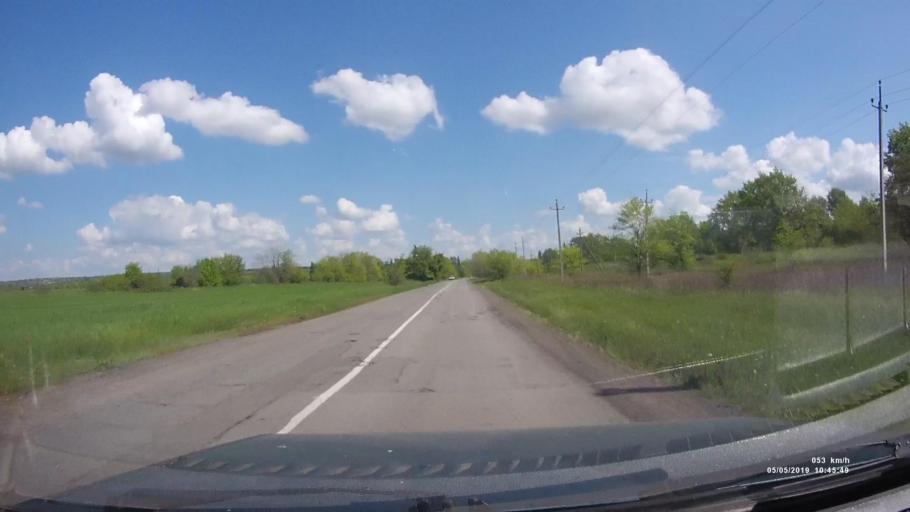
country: RU
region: Rostov
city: Ust'-Donetskiy
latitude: 47.6300
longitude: 40.8400
